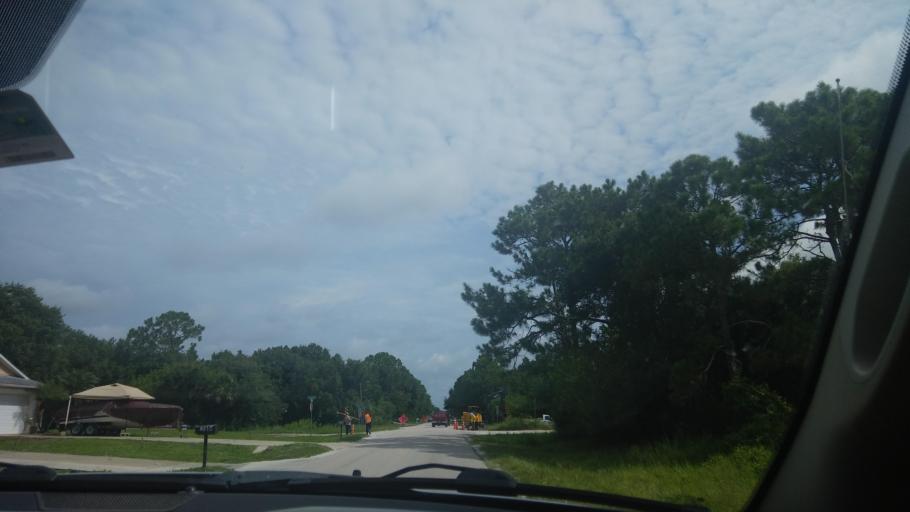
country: US
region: Florida
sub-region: Indian River County
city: Fellsmere
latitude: 27.7557
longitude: -80.5338
